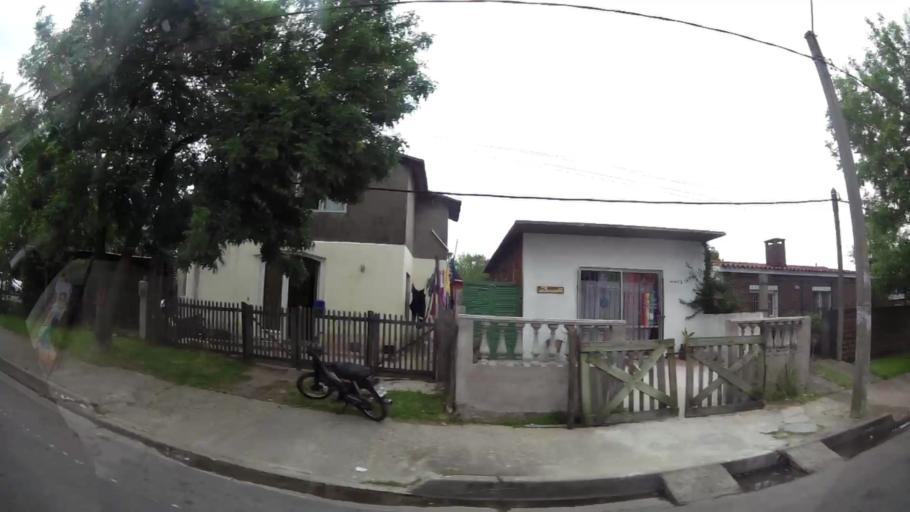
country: UY
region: Maldonado
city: Maldonado
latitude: -34.9052
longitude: -54.9453
